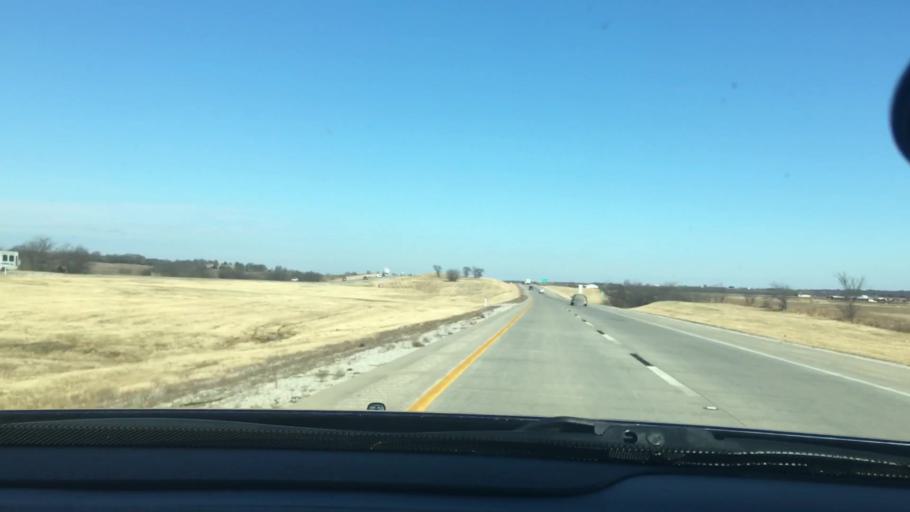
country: US
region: Oklahoma
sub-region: Carter County
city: Ardmore
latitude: 34.0778
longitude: -97.1496
